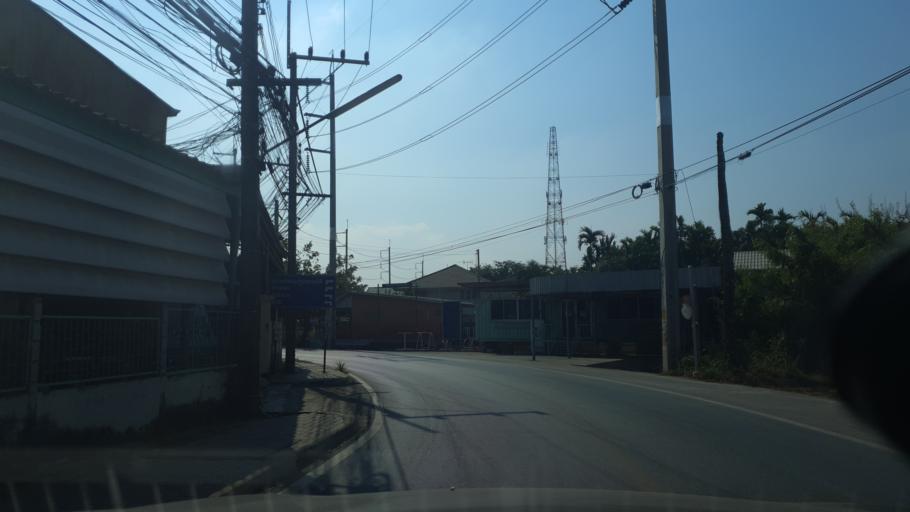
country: TH
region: Nakhon Pathom
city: Salaya
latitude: 13.7844
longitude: 100.2688
